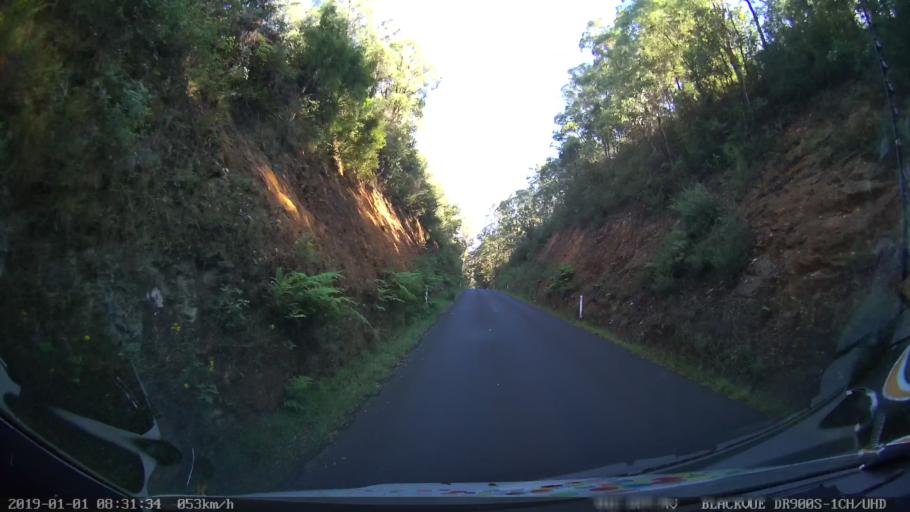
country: AU
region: New South Wales
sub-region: Snowy River
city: Jindabyne
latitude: -36.3692
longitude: 148.2052
